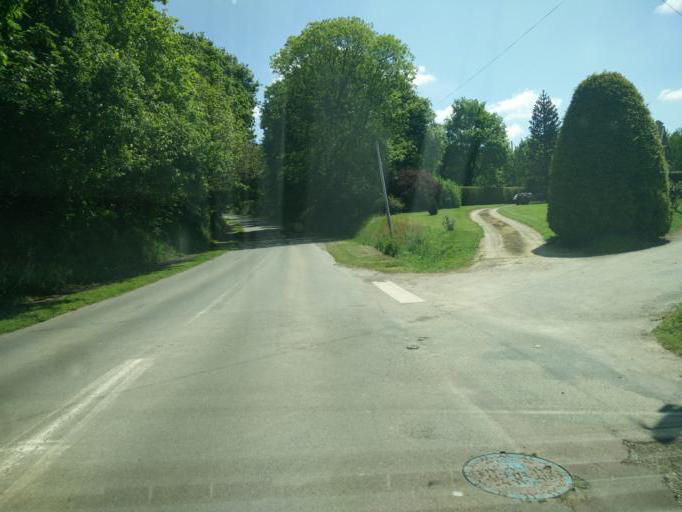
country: FR
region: Brittany
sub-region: Departement du Morbihan
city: Josselin
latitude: 47.9515
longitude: -2.5385
